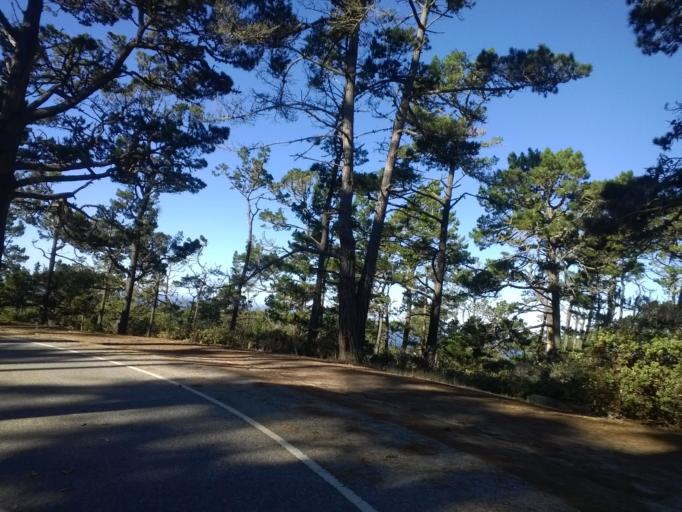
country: US
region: California
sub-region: Monterey County
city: Del Monte Forest
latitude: 36.5853
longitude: -121.9356
